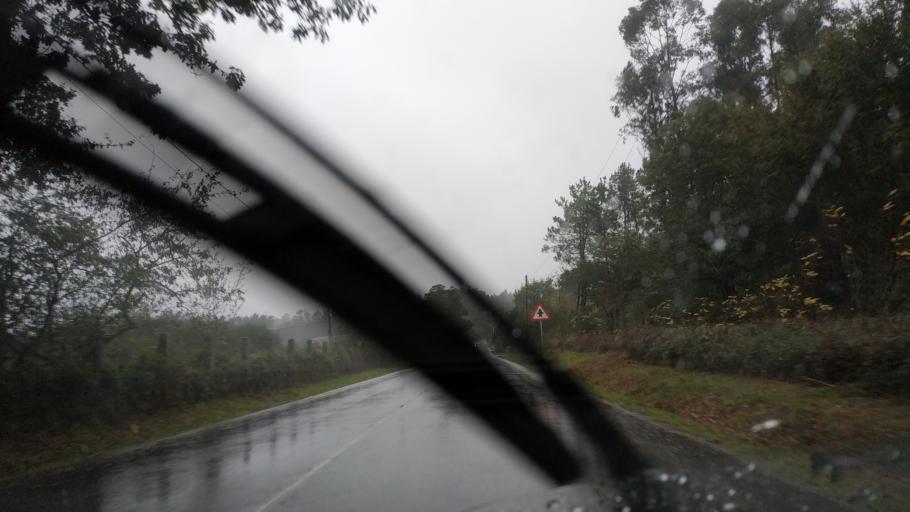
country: ES
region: Galicia
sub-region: Provincia da Coruna
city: Negreira
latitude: 42.9105
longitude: -8.7580
